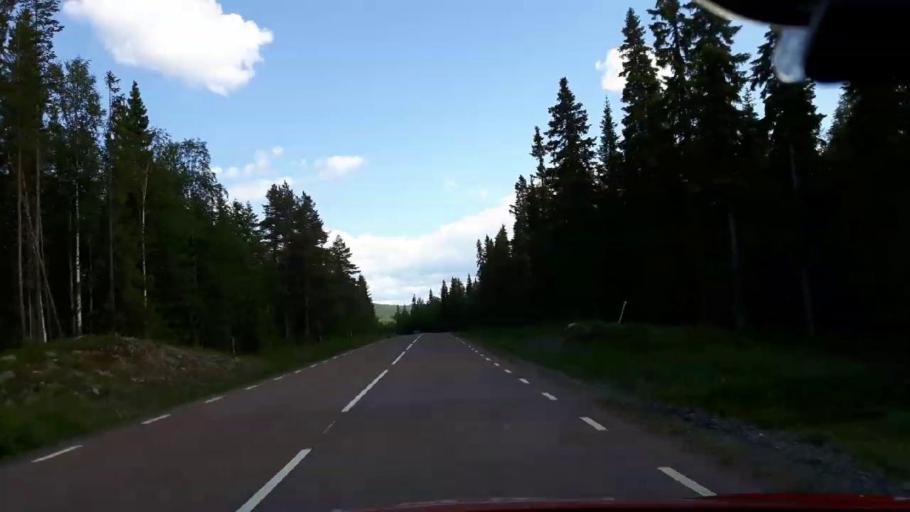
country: SE
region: Jaemtland
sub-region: Krokoms Kommun
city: Valla
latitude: 64.0593
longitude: 14.1550
